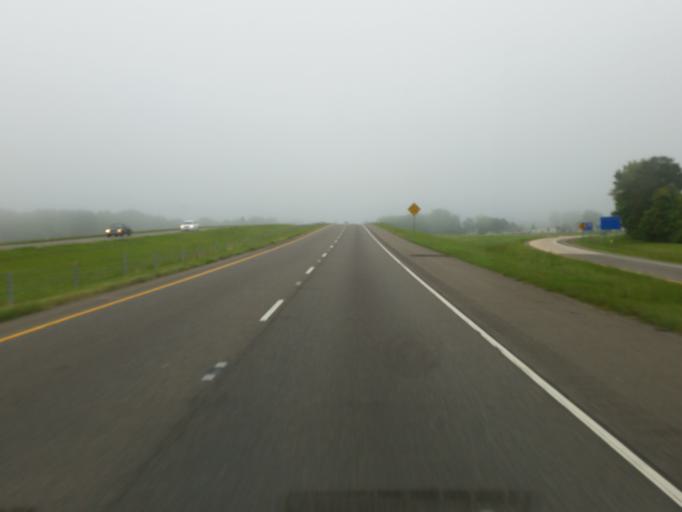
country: US
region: Louisiana
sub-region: Bossier Parish
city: Haughton
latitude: 32.5784
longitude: -93.4358
